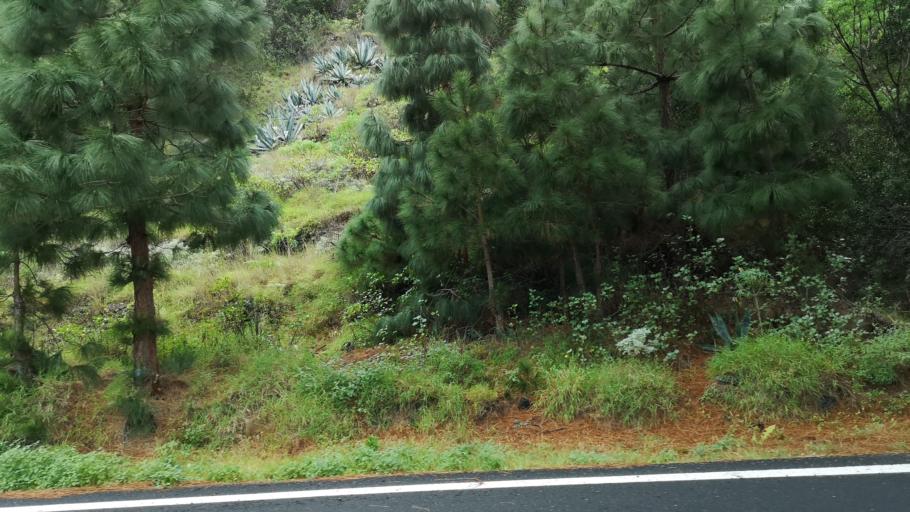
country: ES
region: Canary Islands
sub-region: Provincia de Santa Cruz de Tenerife
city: Hermigua
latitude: 28.1419
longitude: -17.1976
